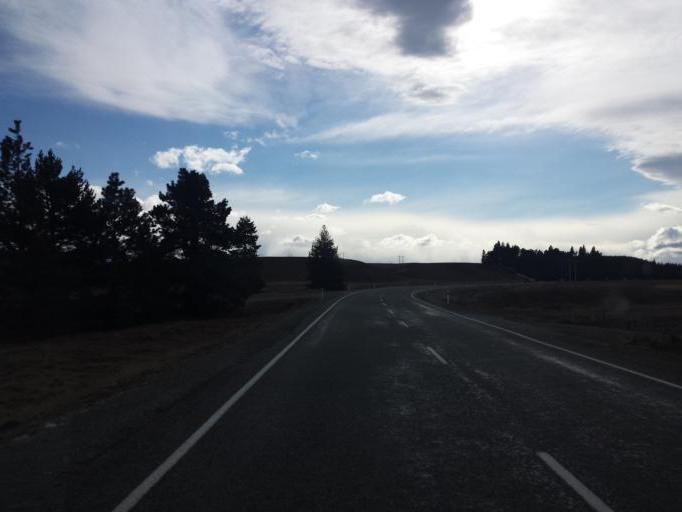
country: NZ
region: Canterbury
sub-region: Timaru District
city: Pleasant Point
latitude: -44.0577
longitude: 170.5022
